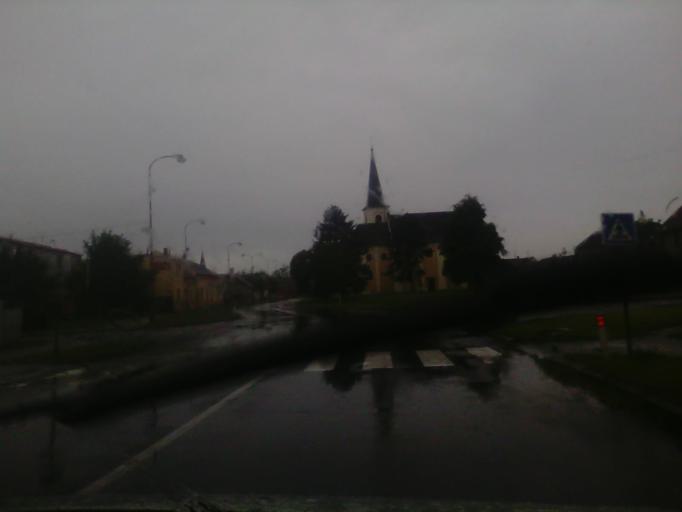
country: CZ
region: Olomoucky
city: Litovel
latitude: 49.7089
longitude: 17.0741
